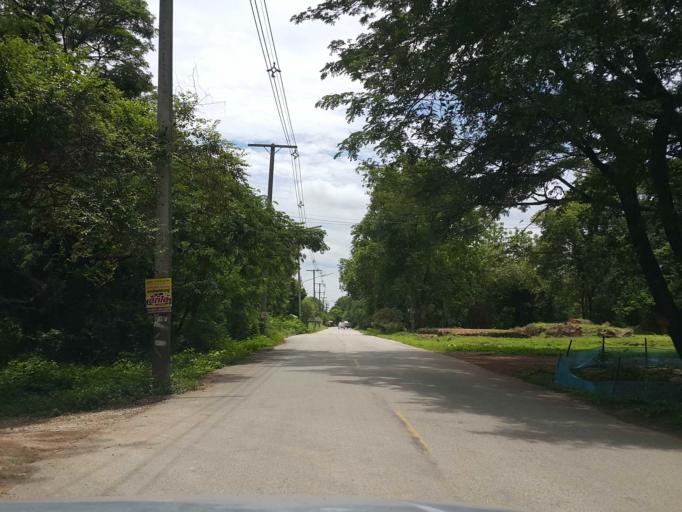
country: TH
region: Sukhothai
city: Ban Na
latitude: 17.0108
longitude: 99.7061
